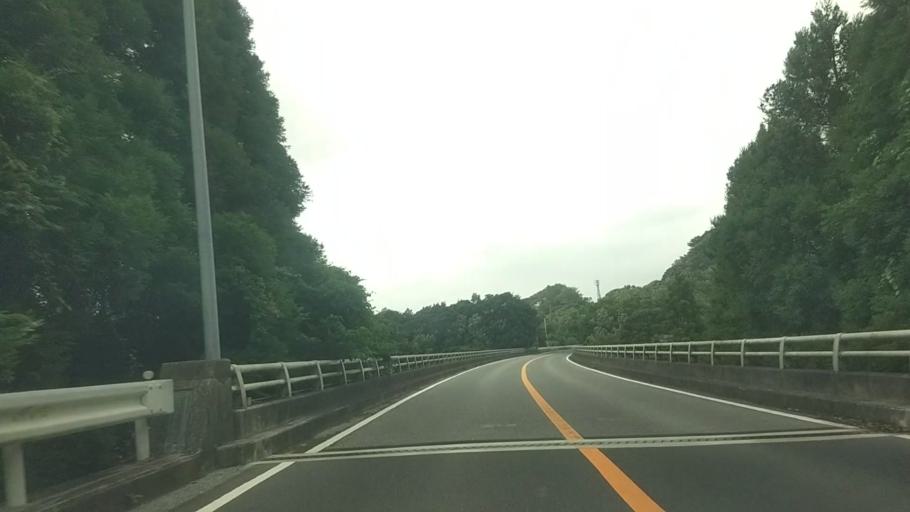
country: JP
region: Chiba
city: Kawaguchi
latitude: 35.2260
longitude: 140.0322
